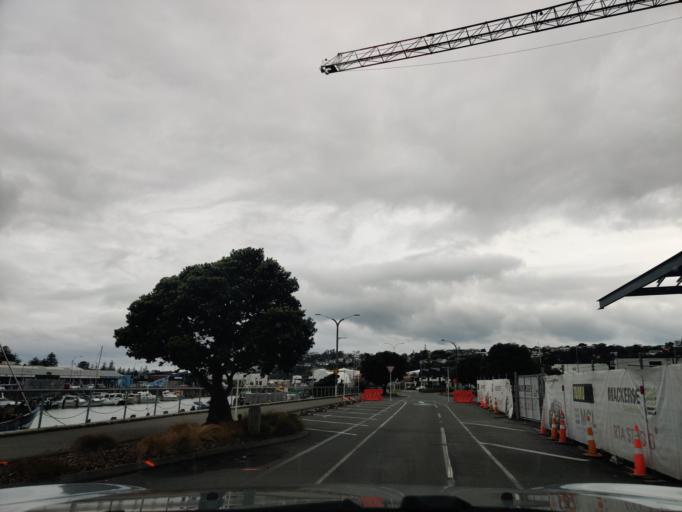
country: NZ
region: Hawke's Bay
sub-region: Napier City
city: Napier
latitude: -39.4818
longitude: 176.8949
